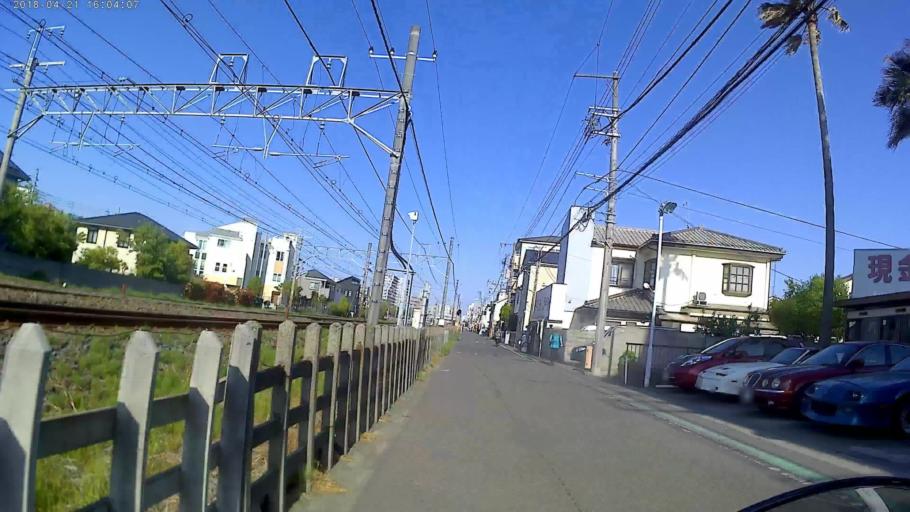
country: JP
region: Kanagawa
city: Fujisawa
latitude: 35.3363
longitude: 139.4378
